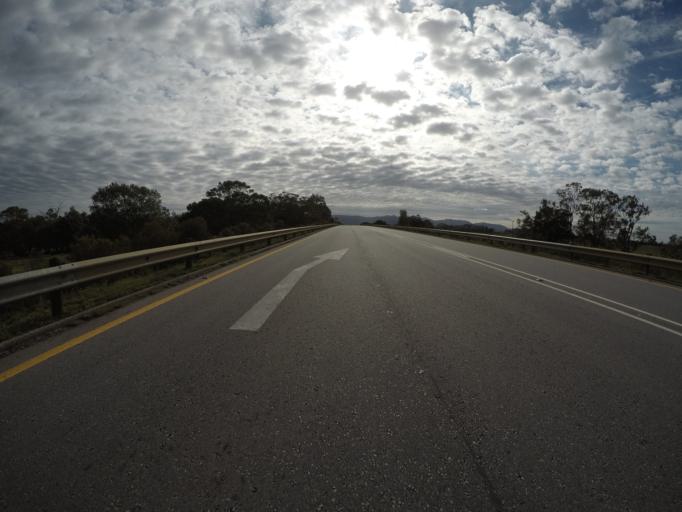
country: ZA
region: Eastern Cape
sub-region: Cacadu District Municipality
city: Kruisfontein
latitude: -34.0369
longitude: 24.5913
